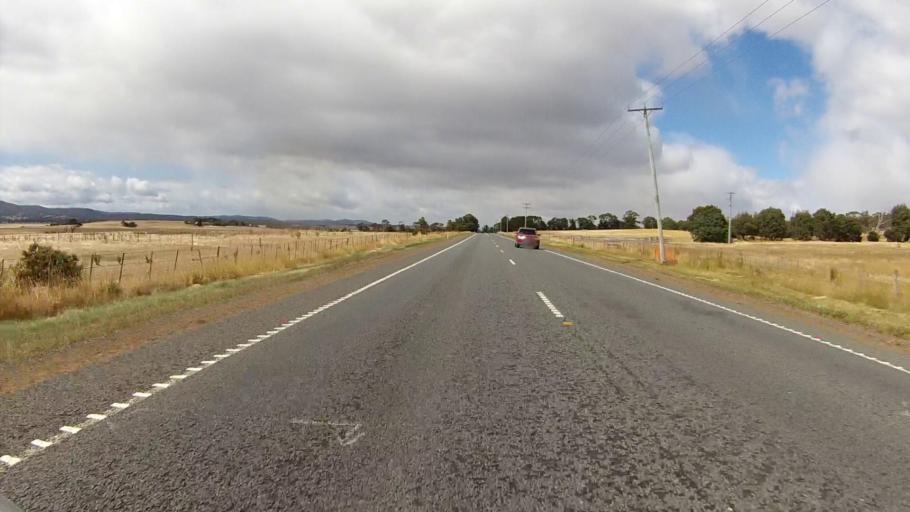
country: AU
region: Tasmania
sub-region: Northern Midlands
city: Evandale
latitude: -41.9778
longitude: 147.5042
